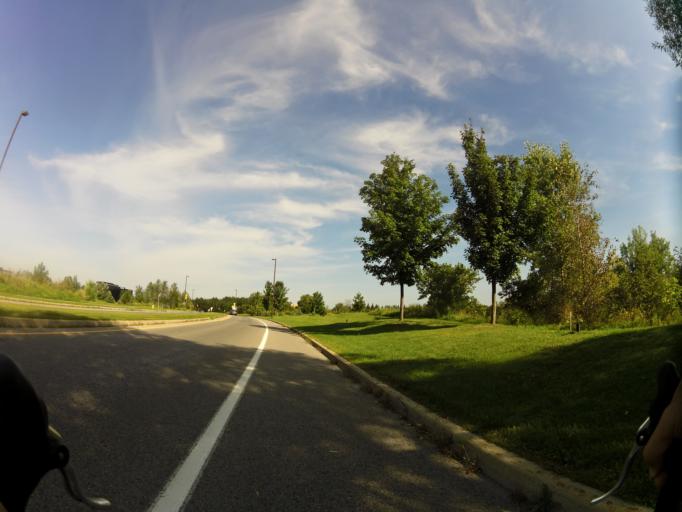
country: CA
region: Ontario
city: Bells Corners
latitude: 45.3464
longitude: -75.9015
